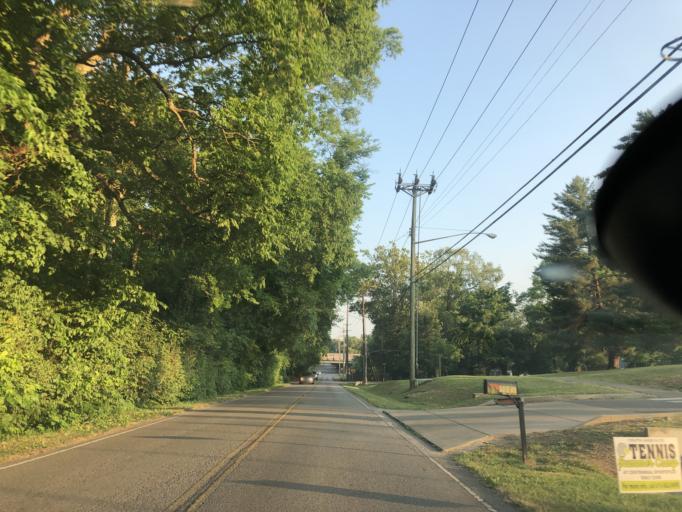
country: US
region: Tennessee
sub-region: Davidson County
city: Oak Hill
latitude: 36.1188
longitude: -86.7873
